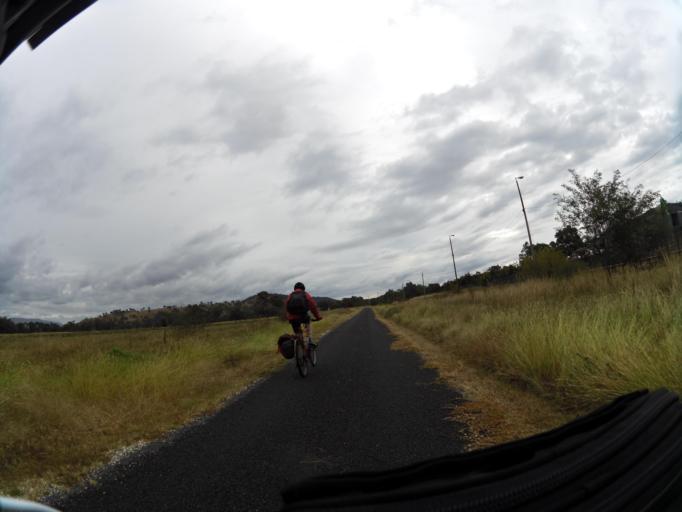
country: AU
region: Victoria
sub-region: Wodonga
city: Wodonga
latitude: -36.1501
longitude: 146.9421
